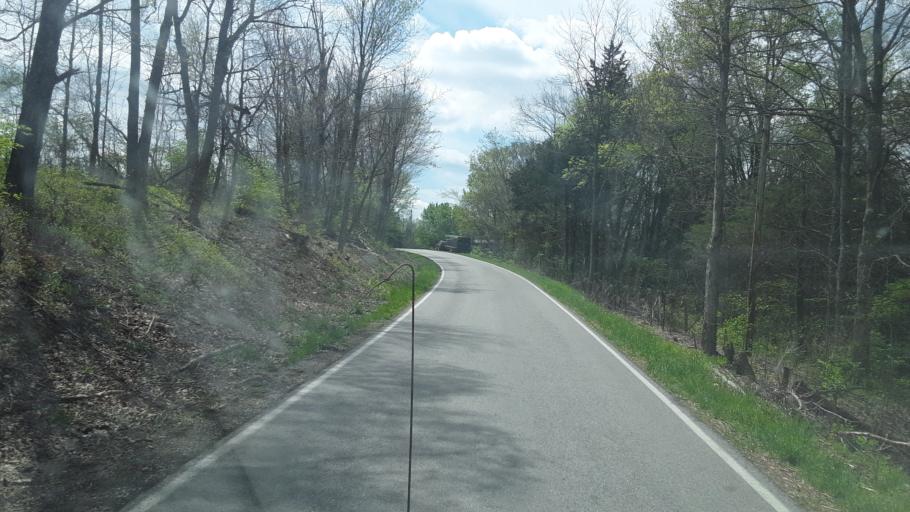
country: US
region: Kentucky
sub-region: Owen County
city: Owenton
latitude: 38.6617
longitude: -84.7713
